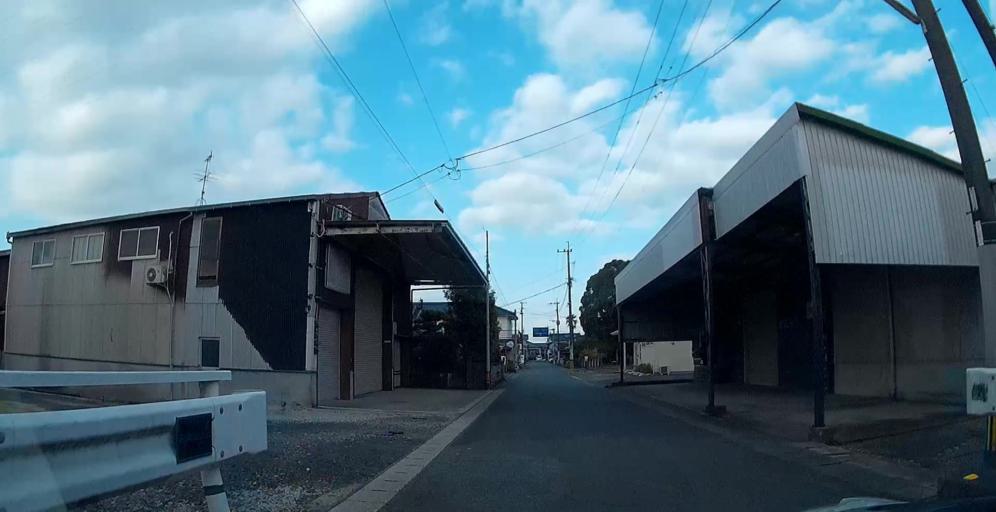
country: JP
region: Kumamoto
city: Yatsushiro
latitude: 32.5342
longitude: 130.6461
